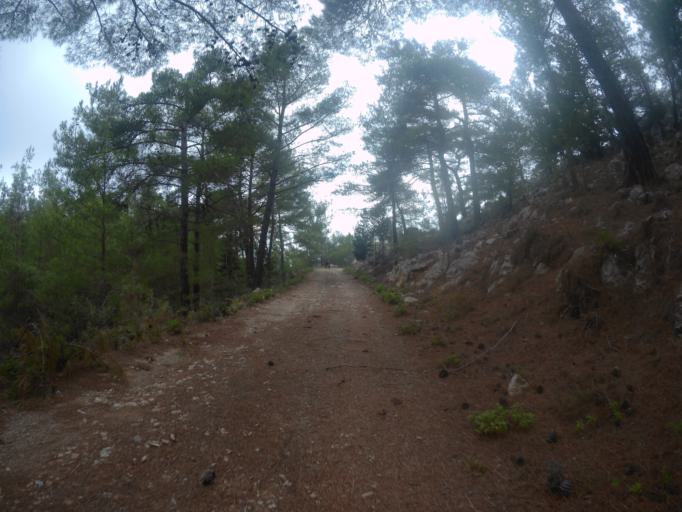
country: CY
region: Ammochostos
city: Lefkonoiko
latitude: 35.2942
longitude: 33.5517
